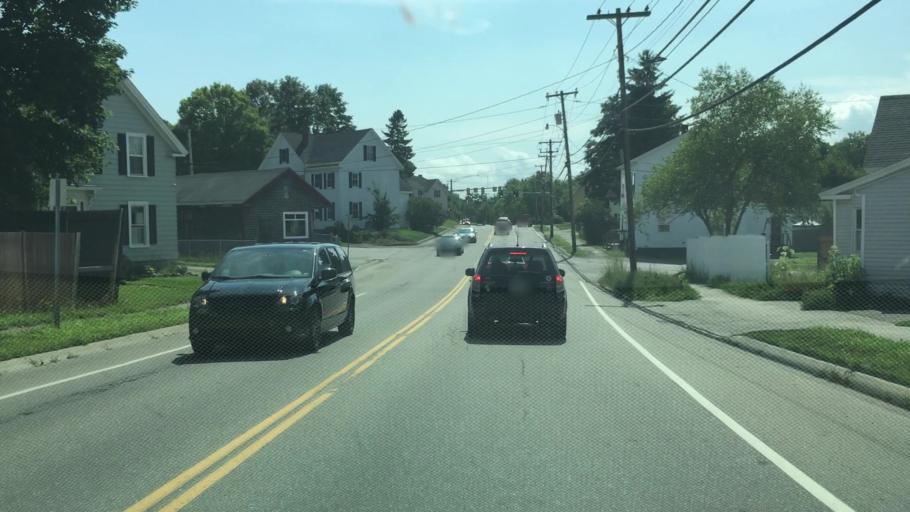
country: US
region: Maine
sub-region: Penobscot County
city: Bangor
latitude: 44.8144
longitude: -68.7668
